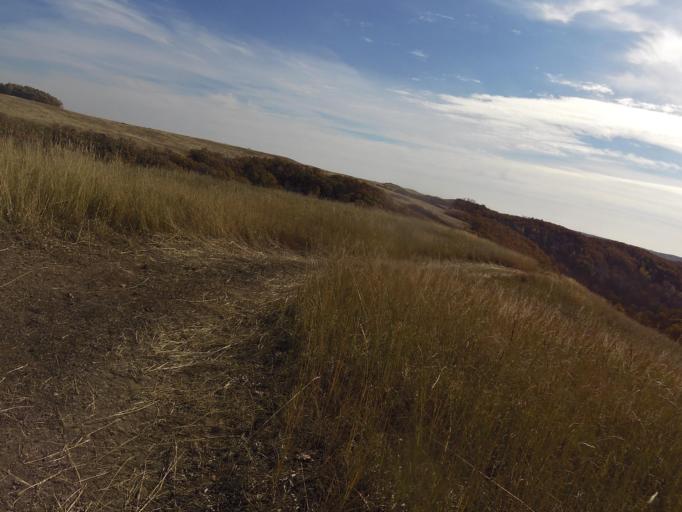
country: CA
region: Manitoba
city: Morden
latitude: 48.9481
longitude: -98.0668
